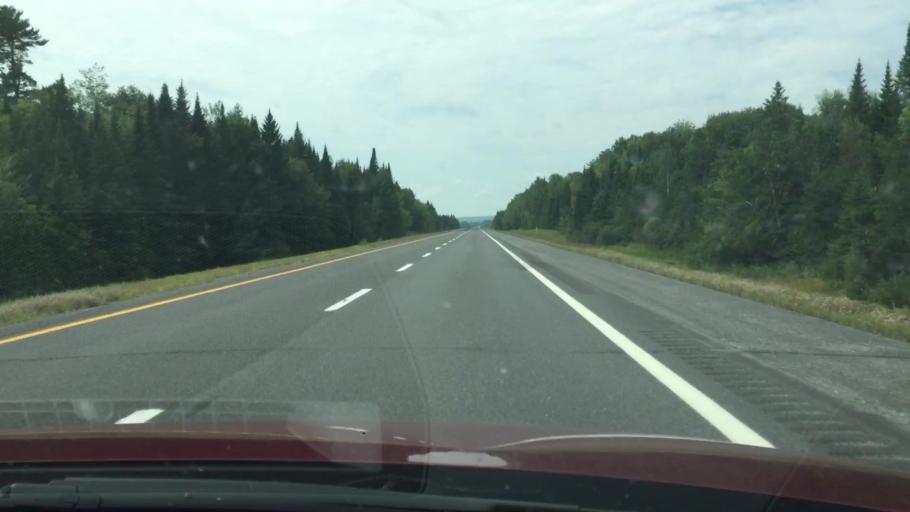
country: US
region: Maine
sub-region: Aroostook County
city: Houlton
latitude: 46.1414
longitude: -67.9637
